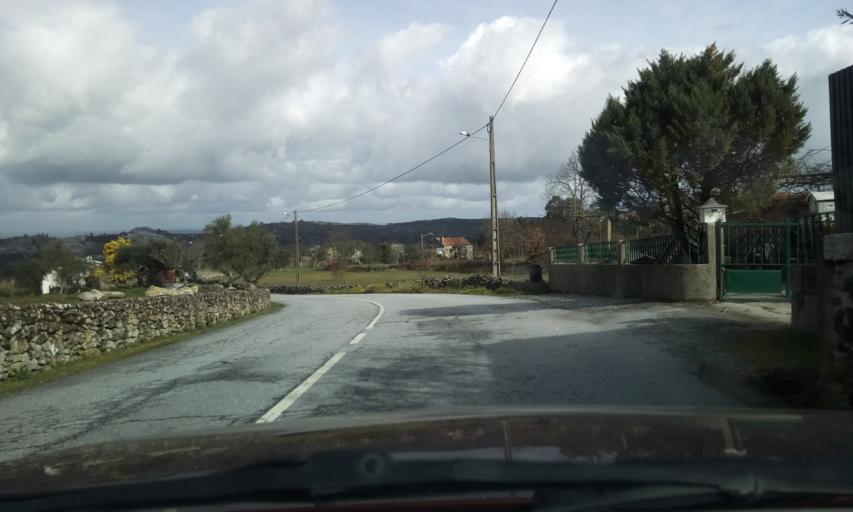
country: PT
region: Guarda
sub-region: Fornos de Algodres
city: Fornos de Algodres
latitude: 40.6521
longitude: -7.5491
